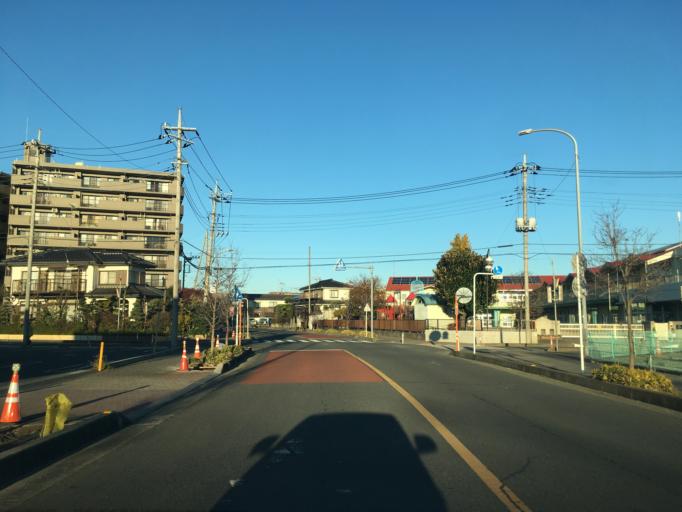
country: JP
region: Saitama
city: Sayama
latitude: 35.8192
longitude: 139.4067
